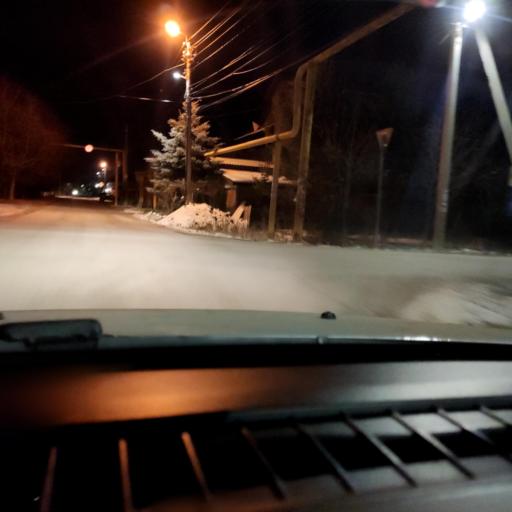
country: RU
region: Samara
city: Podstepki
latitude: 53.5170
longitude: 49.1737
